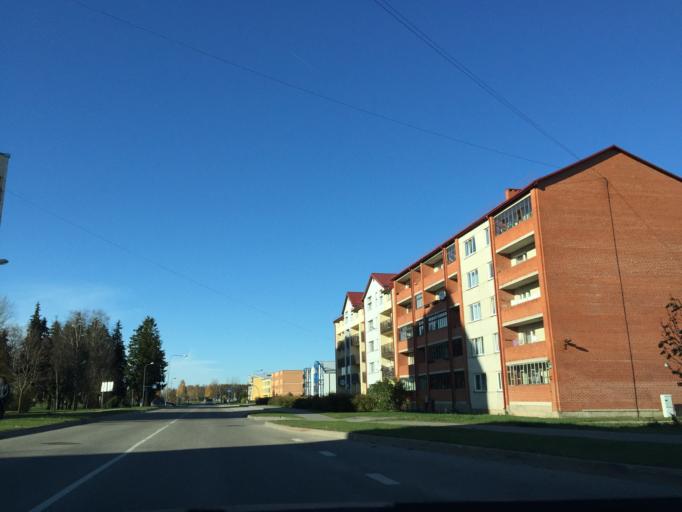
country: LV
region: Aizkraukles Rajons
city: Aizkraukle
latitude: 56.6055
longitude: 25.2634
